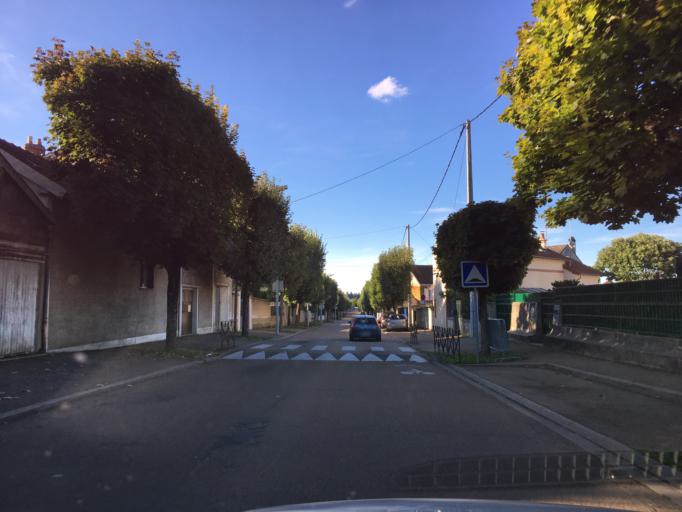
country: FR
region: Bourgogne
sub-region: Departement de l'Yonne
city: Auxerre
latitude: 47.7922
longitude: 3.5607
